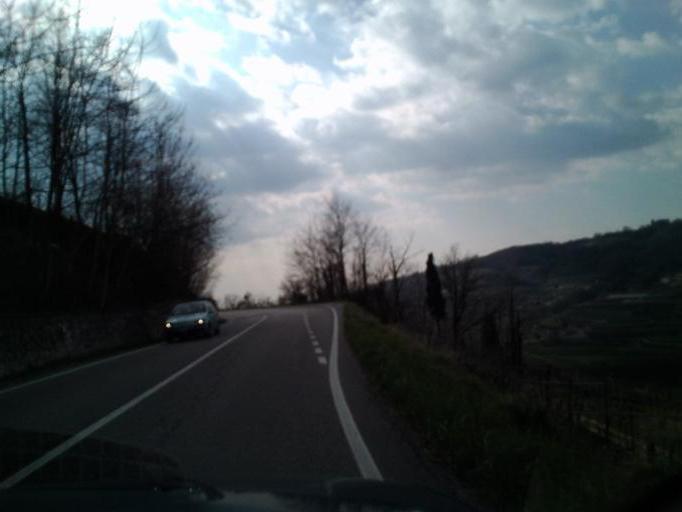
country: IT
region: Veneto
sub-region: Provincia di Verona
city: Fane
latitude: 45.5647
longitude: 10.9582
